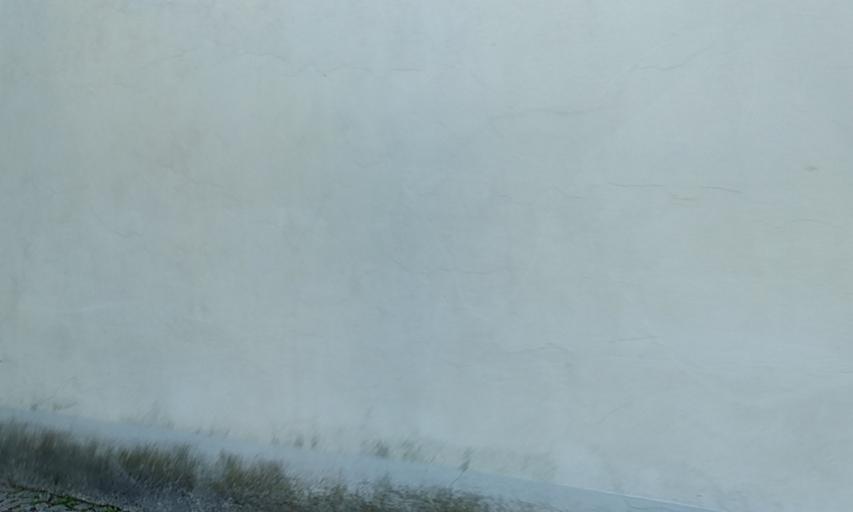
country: PT
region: Evora
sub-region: Evora
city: Evora
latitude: 38.5690
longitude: -7.9141
